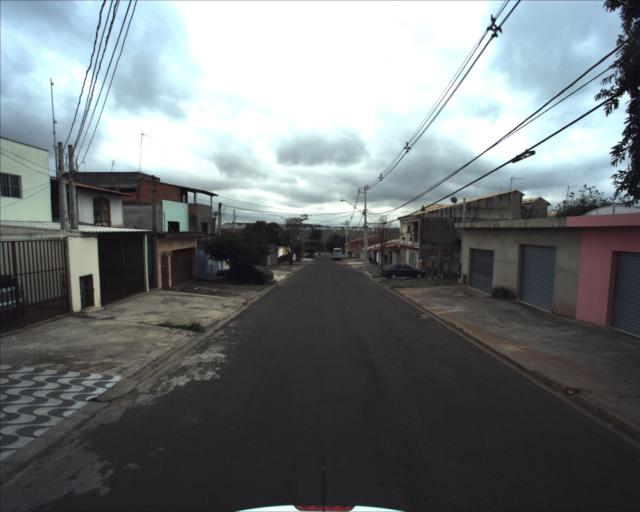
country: BR
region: Sao Paulo
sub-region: Sorocaba
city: Sorocaba
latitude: -23.4322
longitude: -47.5090
